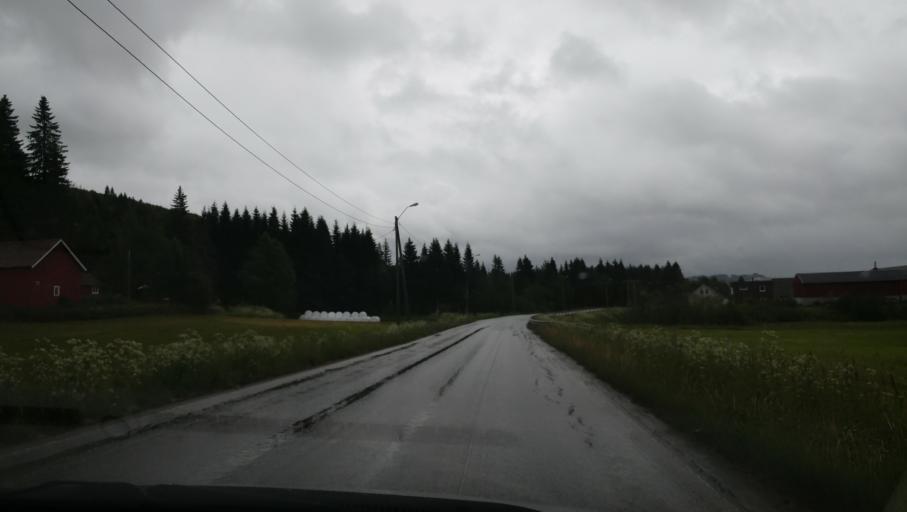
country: NO
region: Sor-Trondelag
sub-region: Selbu
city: Mebonden
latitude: 63.2803
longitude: 11.0807
